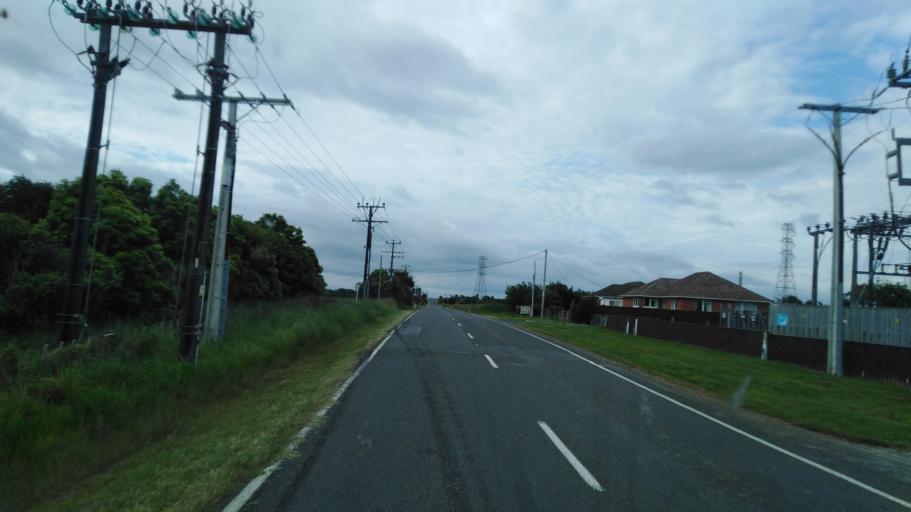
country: NZ
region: Manawatu-Wanganui
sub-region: Rangitikei District
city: Bulls
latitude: -40.1026
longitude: 175.3614
